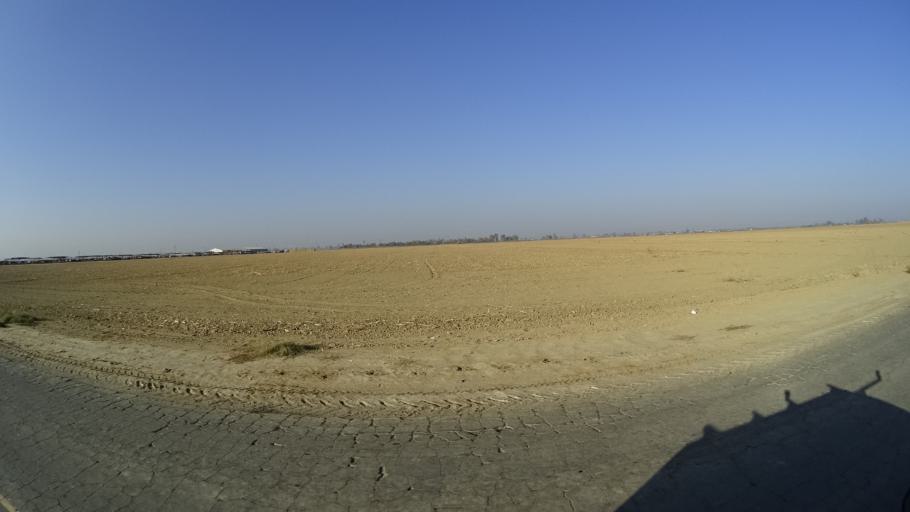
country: US
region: California
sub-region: Kern County
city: Greenfield
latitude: 35.2340
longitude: -118.9677
